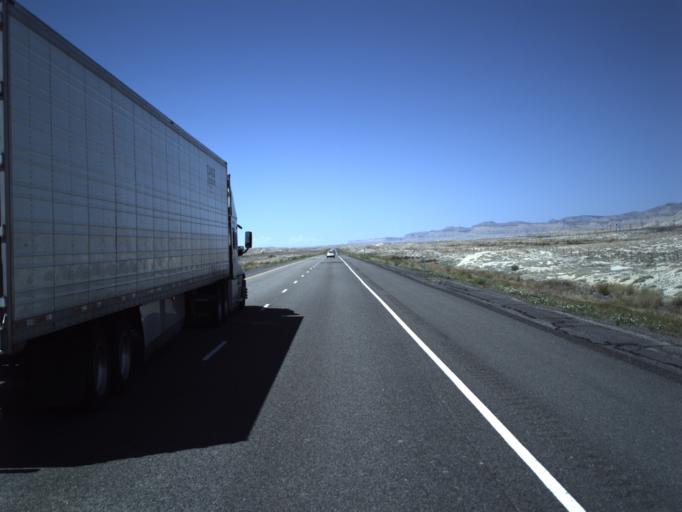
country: US
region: Utah
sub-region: Grand County
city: Moab
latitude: 38.9350
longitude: -109.4531
